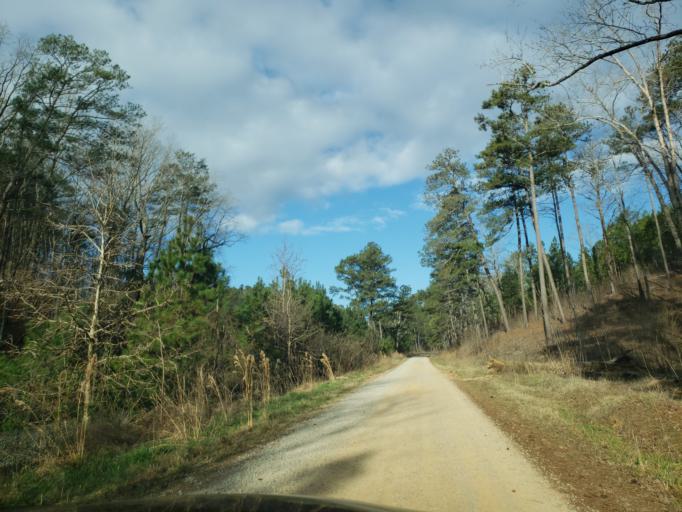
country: US
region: Alabama
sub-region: Cleburne County
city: Heflin
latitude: 33.6492
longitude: -85.6327
